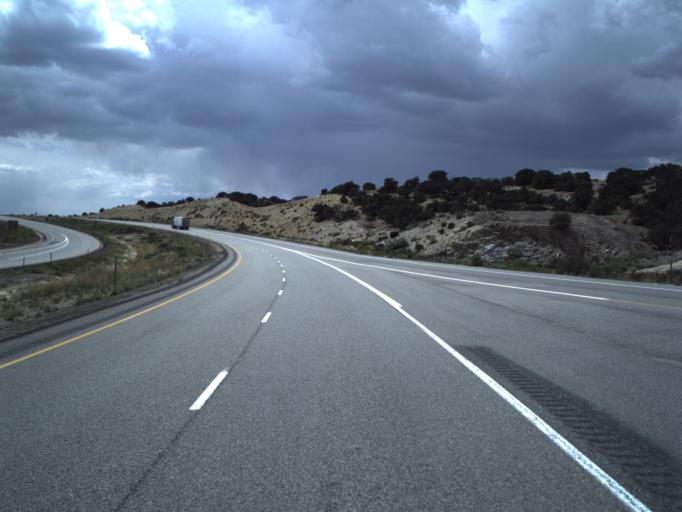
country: US
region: Utah
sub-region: Emery County
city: Ferron
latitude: 38.8559
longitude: -110.9187
